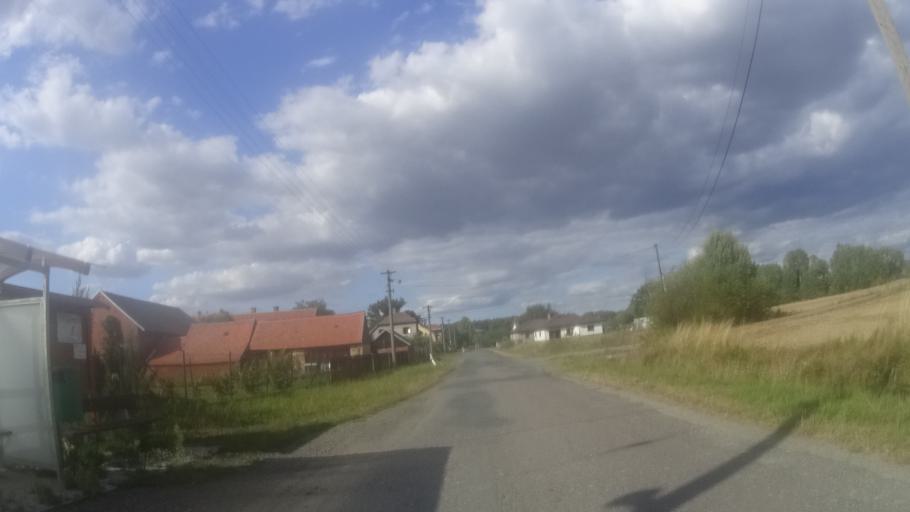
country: CZ
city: Albrechtice nad Orlici
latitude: 50.1685
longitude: 16.0308
